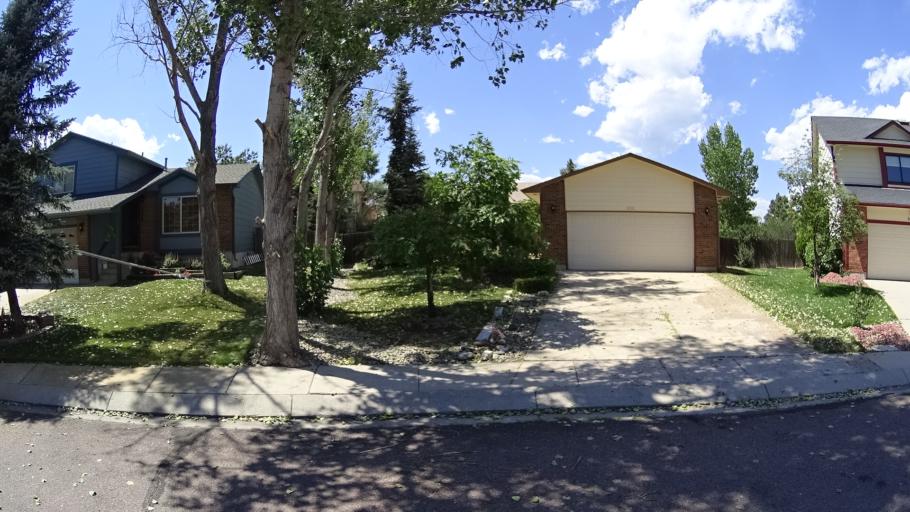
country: US
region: Colorado
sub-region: El Paso County
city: Black Forest
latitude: 38.9491
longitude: -104.7466
